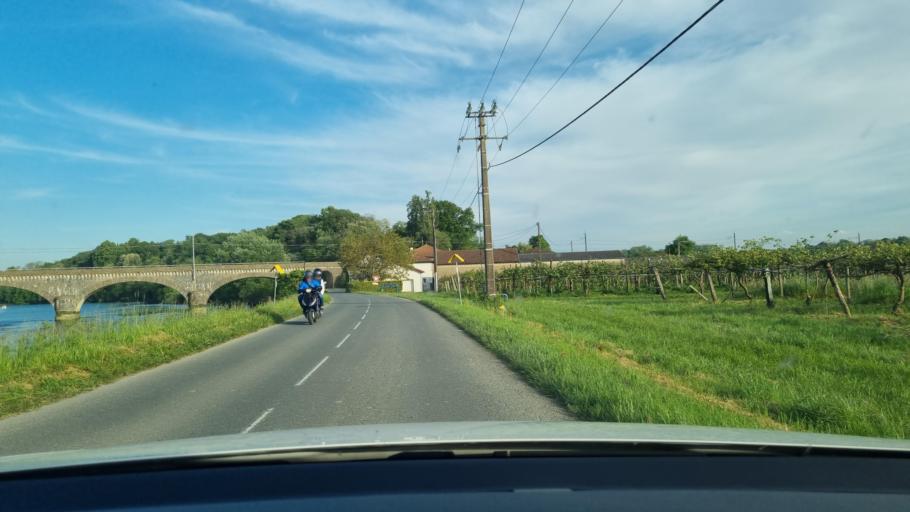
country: FR
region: Aquitaine
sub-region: Departement des Landes
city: Peyrehorade
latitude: 43.5390
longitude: -1.1611
